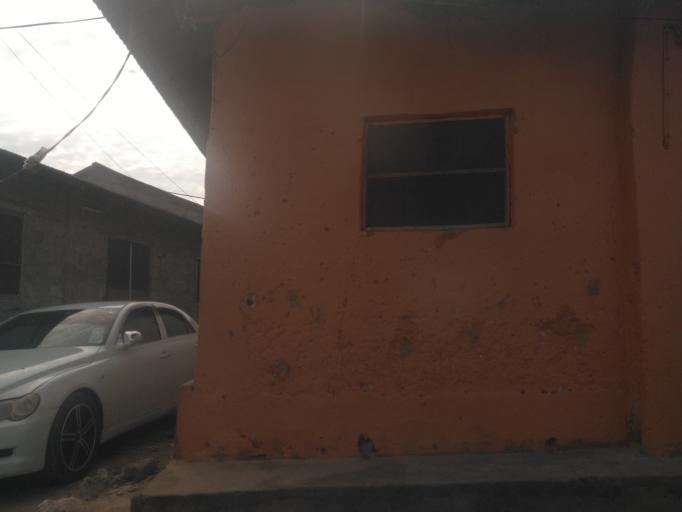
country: TZ
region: Zanzibar Urban/West
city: Zanzibar
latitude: -6.1630
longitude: 39.2014
